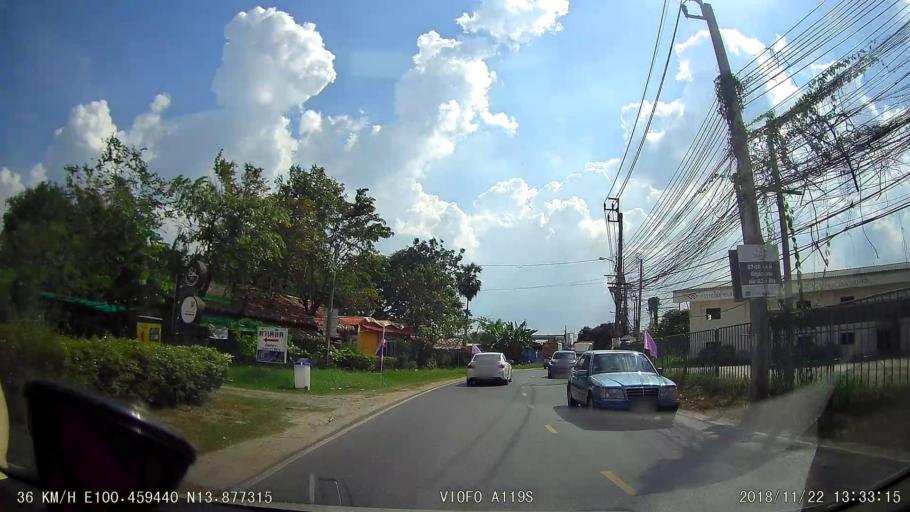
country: TH
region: Nonthaburi
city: Bang Bua Thong
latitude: 13.8772
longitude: 100.4595
